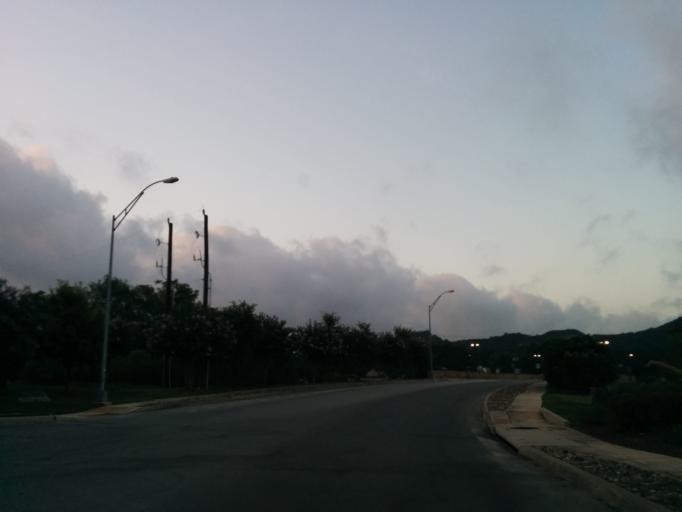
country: US
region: Texas
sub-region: Bexar County
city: Cross Mountain
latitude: 29.6682
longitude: -98.6391
